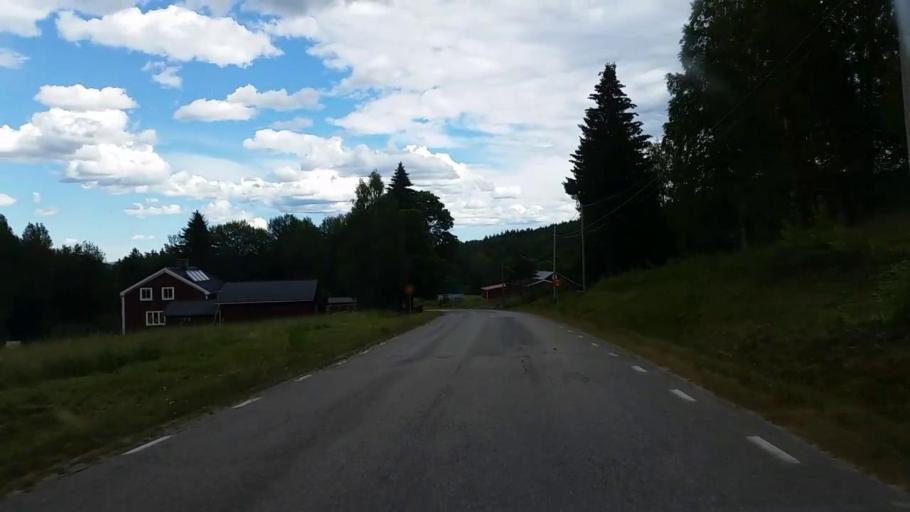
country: SE
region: Gaevleborg
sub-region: Ljusdals Kommun
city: Jaervsoe
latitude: 61.6674
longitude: 16.0822
